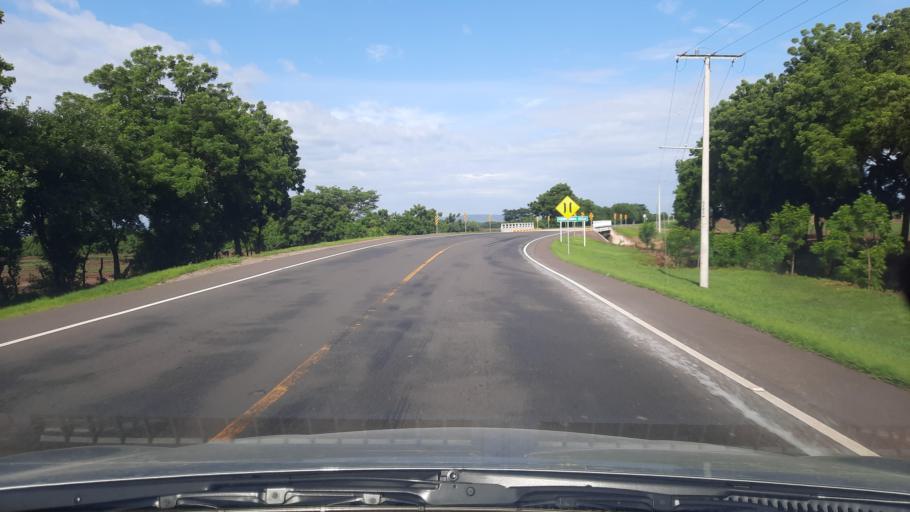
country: NI
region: Chinandega
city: Chichigalpa
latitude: 12.7663
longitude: -86.9064
